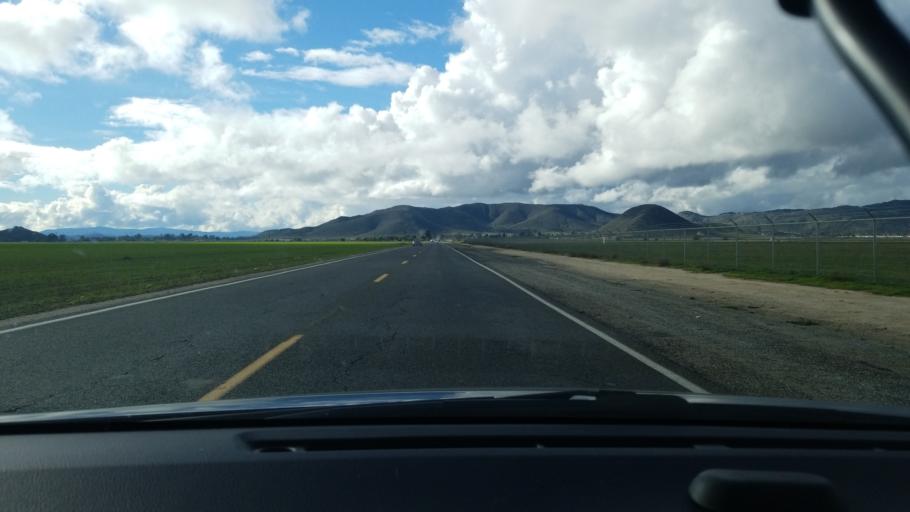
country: US
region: California
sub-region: Riverside County
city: Green Acres
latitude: 33.7293
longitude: -117.0248
